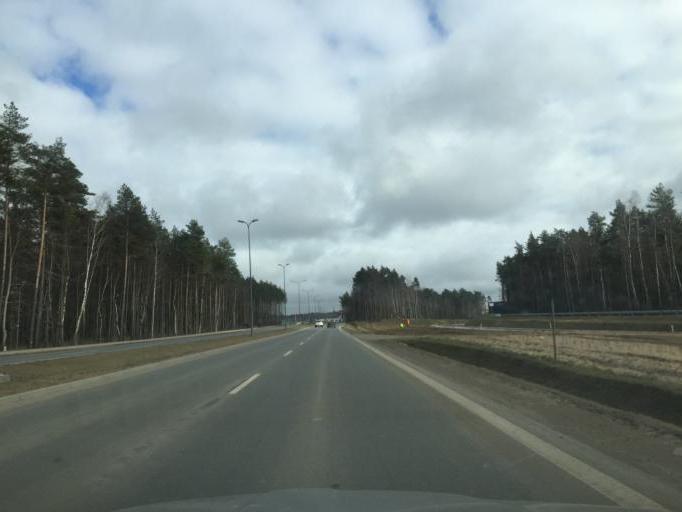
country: PL
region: Pomeranian Voivodeship
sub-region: Gdynia
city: Wielki Kack
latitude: 54.3780
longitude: 18.4964
